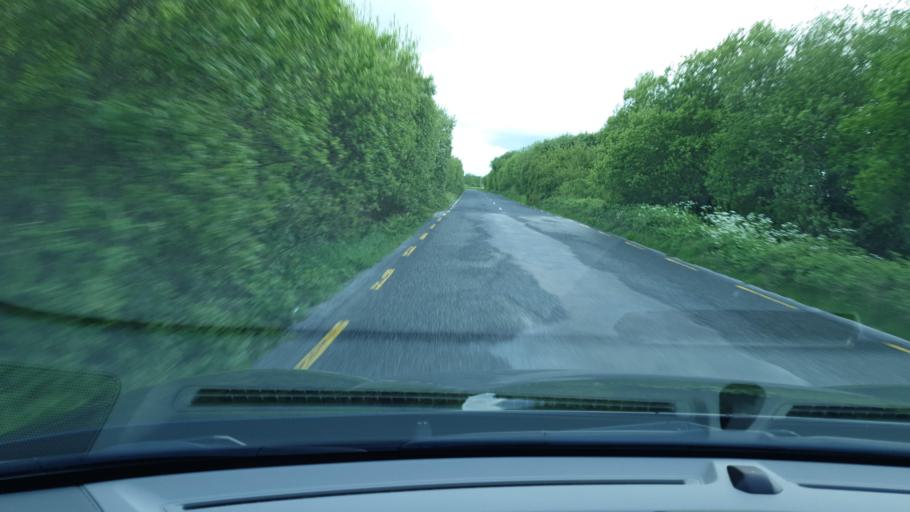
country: IE
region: Leinster
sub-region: Uibh Fhaili
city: Ferbane
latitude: 53.2383
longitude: -7.7006
